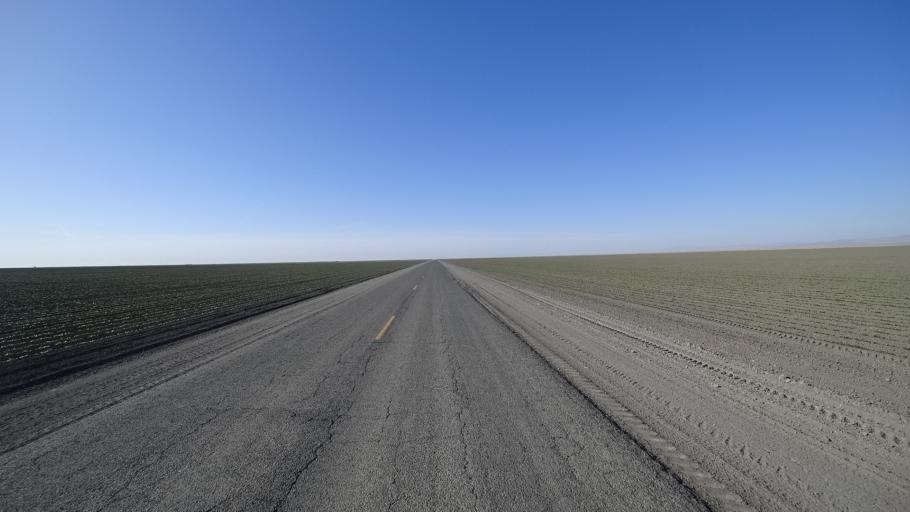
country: US
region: California
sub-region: Kings County
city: Stratford
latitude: 36.0996
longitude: -119.7979
